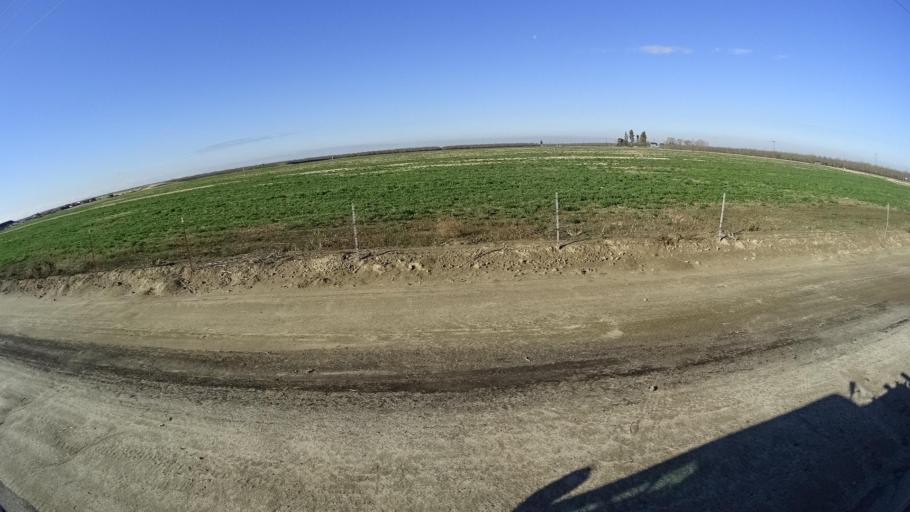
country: US
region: California
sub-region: Kern County
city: McFarland
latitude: 35.6871
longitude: -119.2764
